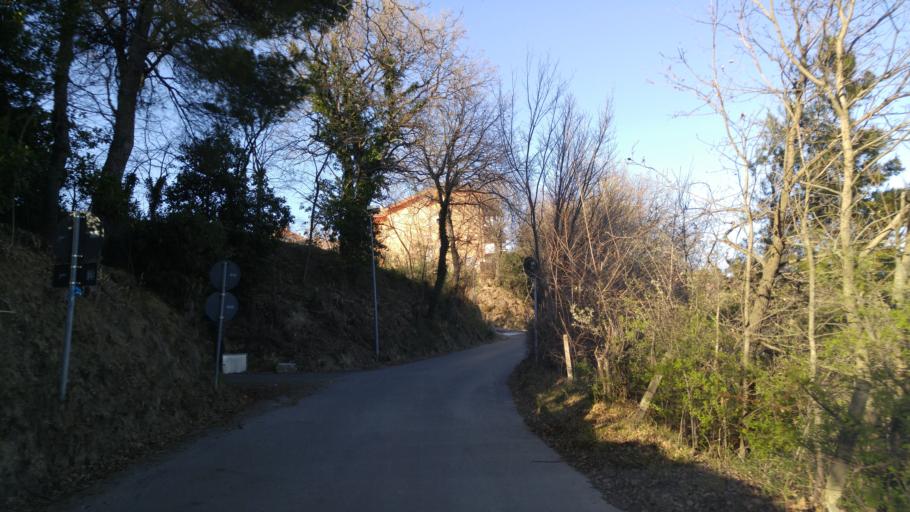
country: IT
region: The Marches
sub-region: Provincia di Pesaro e Urbino
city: Fenile
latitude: 43.8561
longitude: 12.9287
